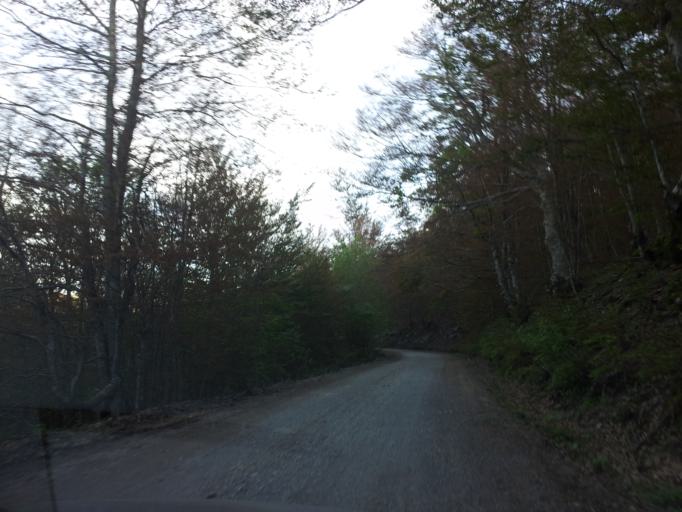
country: HR
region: Zadarska
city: Obrovac
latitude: 44.2920
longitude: 15.6511
